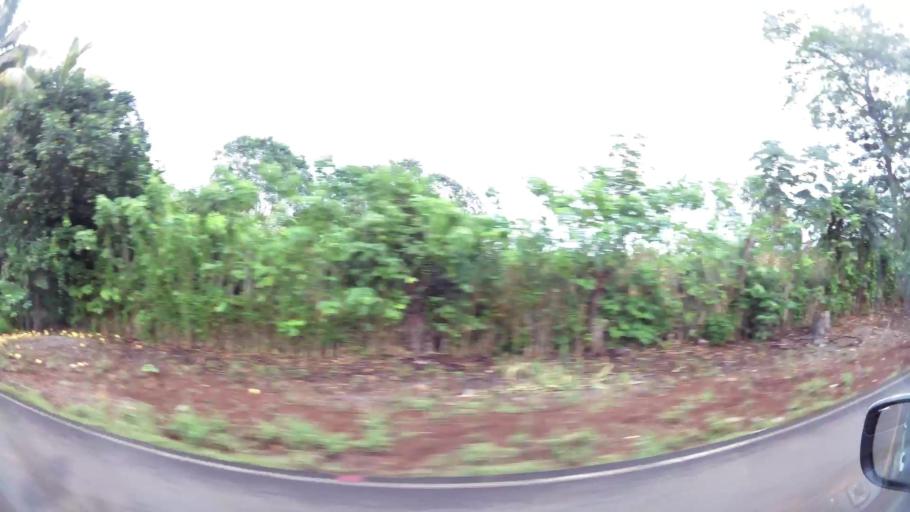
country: CR
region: Puntarenas
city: Esparza
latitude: 9.9709
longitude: -84.6165
